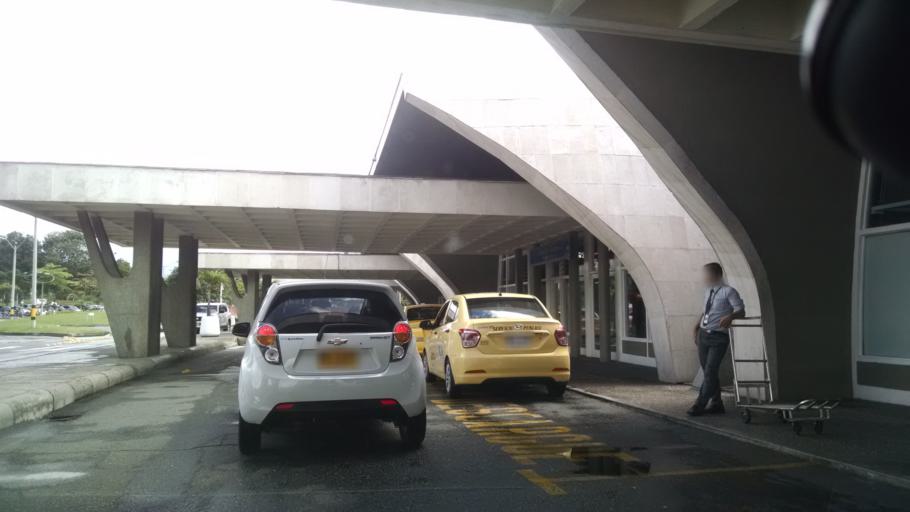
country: CO
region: Antioquia
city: Itagui
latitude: 6.2190
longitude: -75.5864
